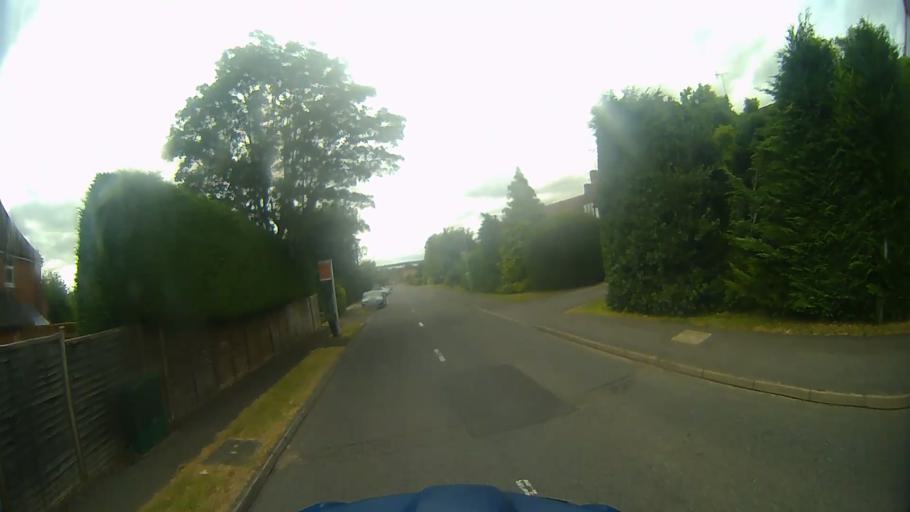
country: GB
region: England
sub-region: Wokingham
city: Earley
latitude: 51.4532
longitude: -0.9283
